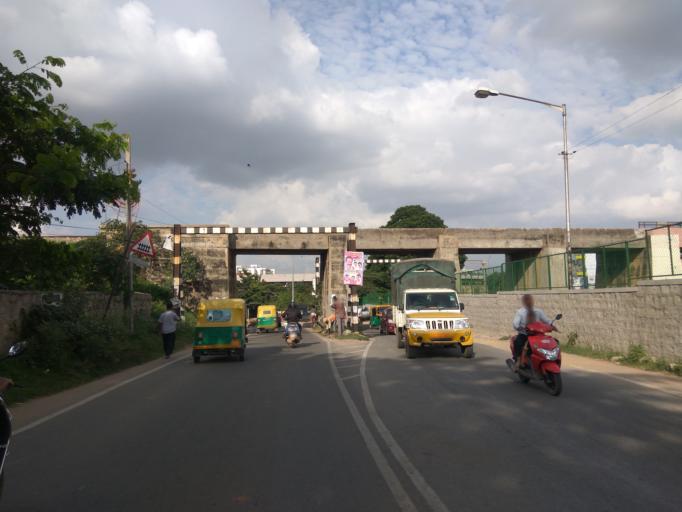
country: IN
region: Karnataka
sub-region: Bangalore Urban
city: Bangalore
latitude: 12.9969
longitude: 77.6623
